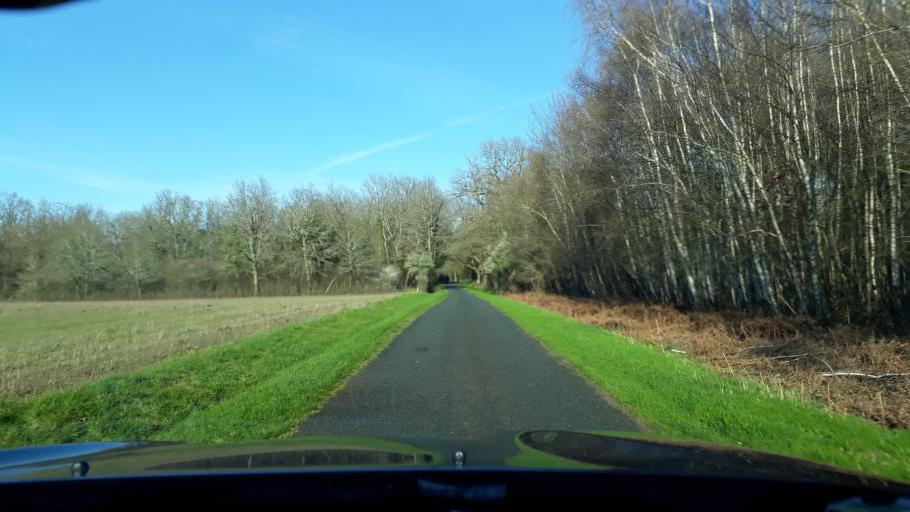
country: FR
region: Centre
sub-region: Departement du Loiret
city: Ligny-le-Ribault
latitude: 47.6909
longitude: 1.7940
